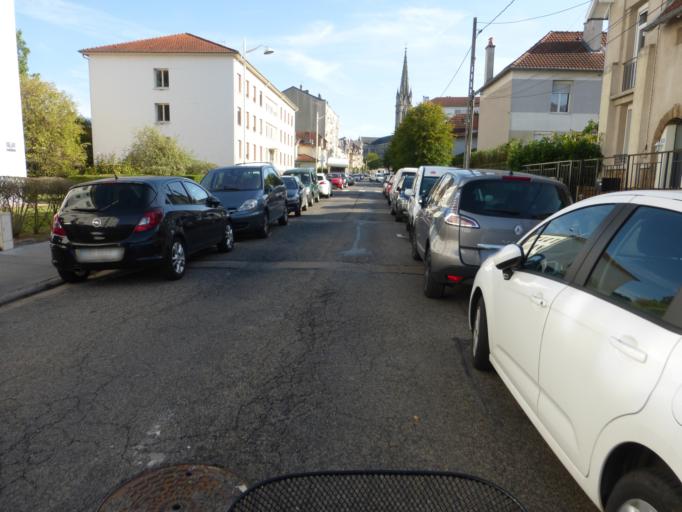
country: FR
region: Lorraine
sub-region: Departement de Meurthe-et-Moselle
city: Nancy
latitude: 48.6763
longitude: 6.1722
